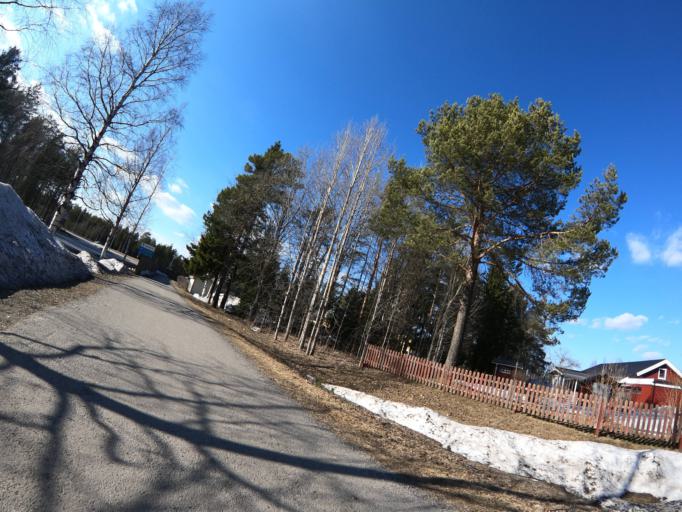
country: SE
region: Vaesterbotten
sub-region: Umea Kommun
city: Umea
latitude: 63.8052
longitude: 20.3238
